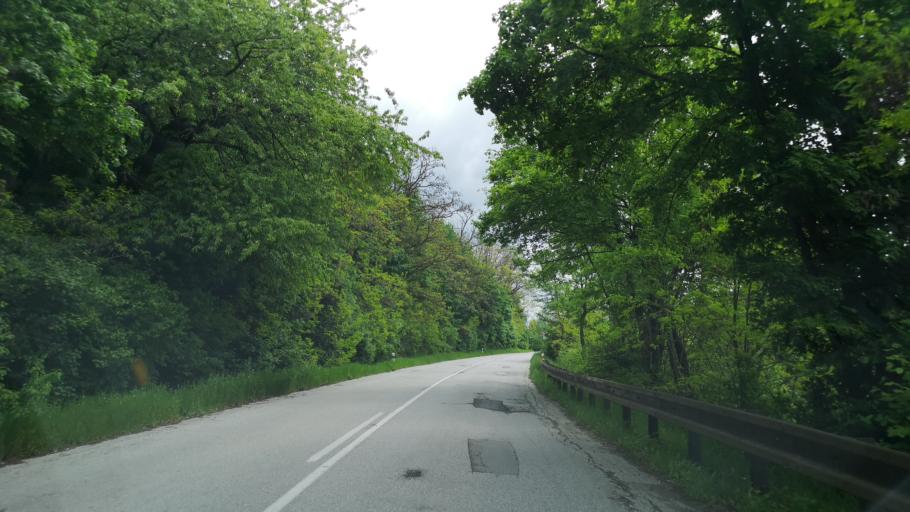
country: SK
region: Kosicky
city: Roznava
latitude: 48.6354
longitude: 20.3568
